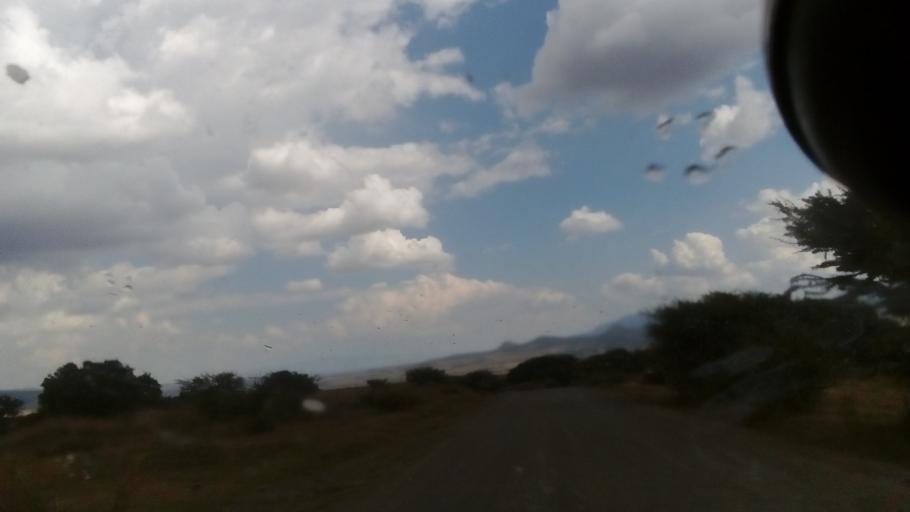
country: MX
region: Guanajuato
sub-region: Leon
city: Lucio Blanco (Los Gavilanes)
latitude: 21.1932
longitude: -101.4762
